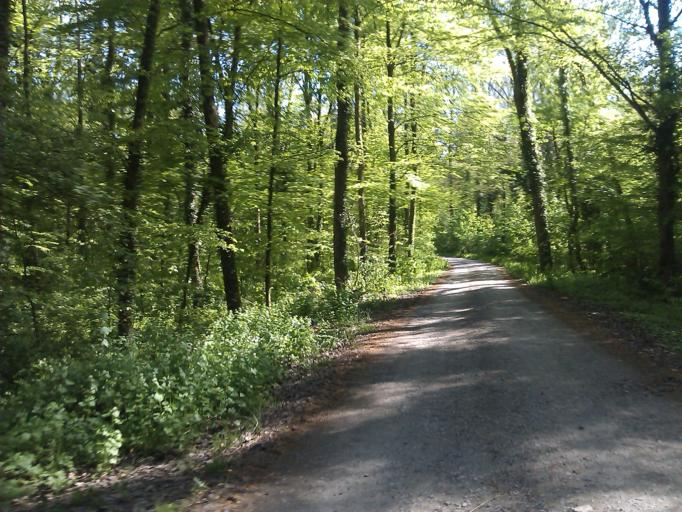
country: DE
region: Baden-Wuerttemberg
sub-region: Karlsruhe Region
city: Sulzfeld
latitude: 49.0901
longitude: 8.8658
